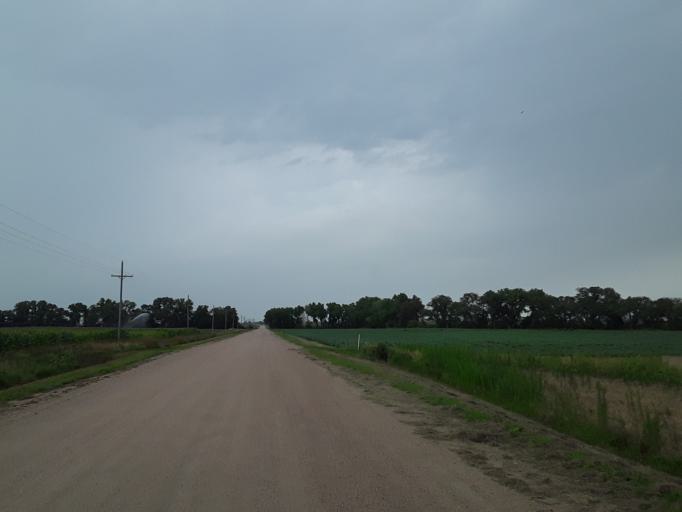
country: US
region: Nebraska
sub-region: Saunders County
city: Yutan
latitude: 41.1624
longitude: -96.4448
